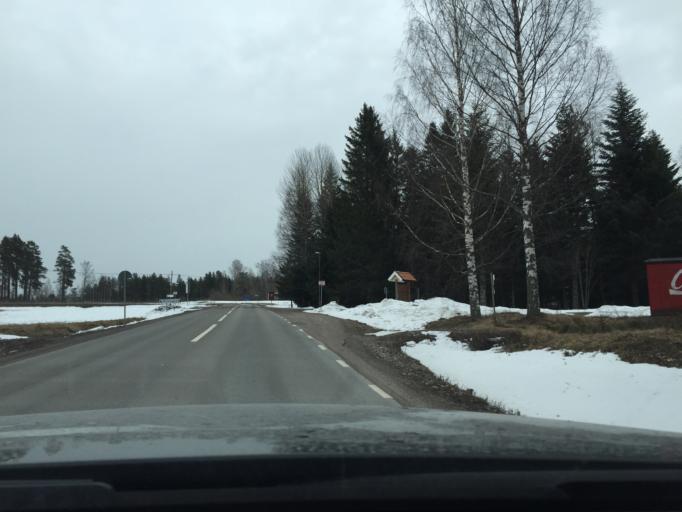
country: SE
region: Gaevleborg
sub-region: Sandvikens Kommun
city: Jarbo
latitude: 60.7598
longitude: 16.5332
